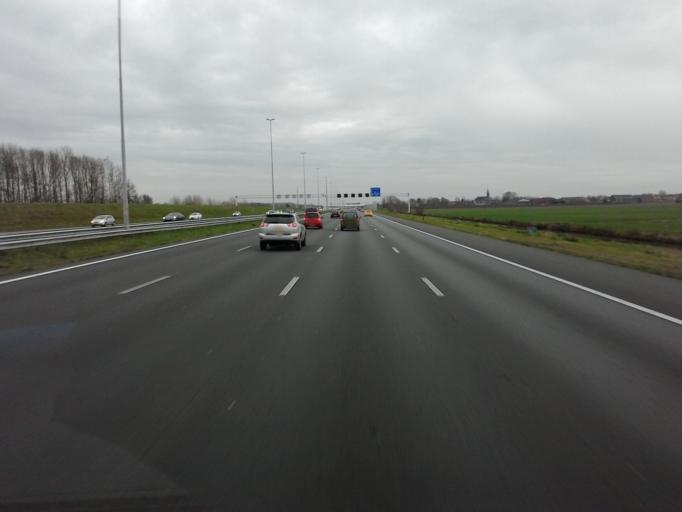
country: NL
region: Utrecht
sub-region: Gemeente Vianen
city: Vianen
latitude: 51.9500
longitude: 5.1331
